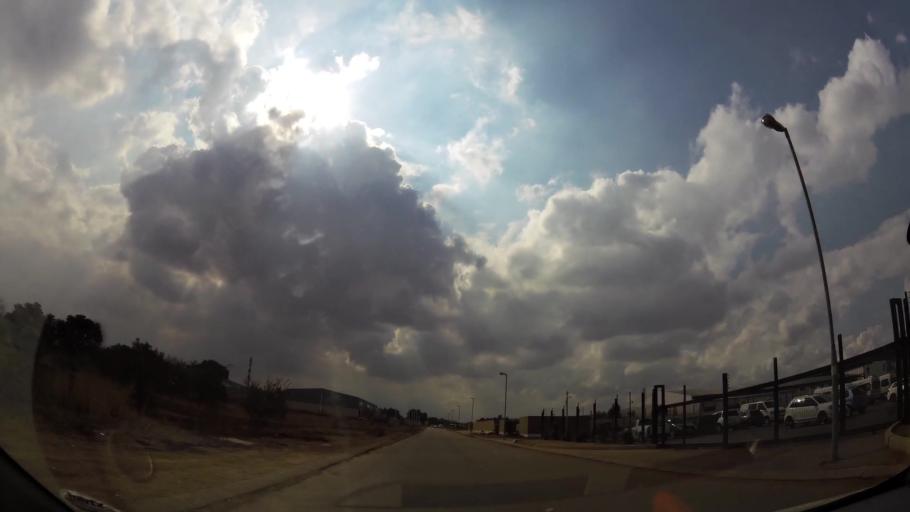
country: ZA
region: Gauteng
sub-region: Sedibeng District Municipality
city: Vereeniging
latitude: -26.6610
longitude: 27.9328
